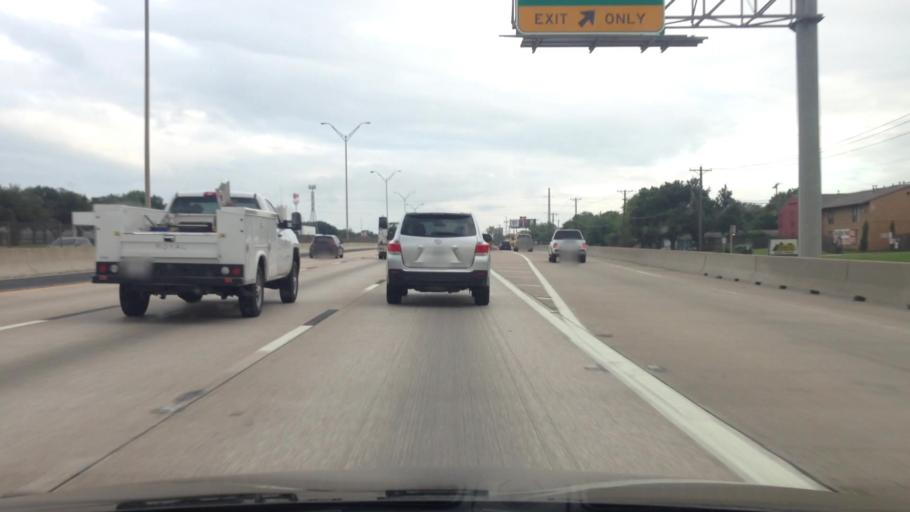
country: US
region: Texas
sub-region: Tarrant County
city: Edgecliff Village
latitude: 32.6504
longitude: -97.3215
